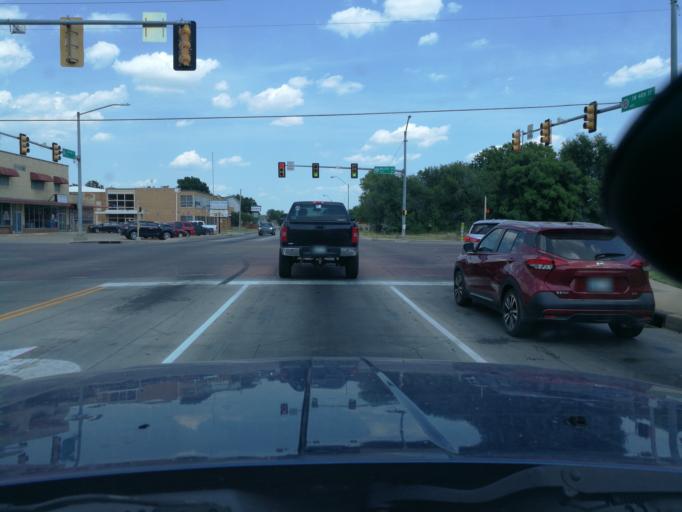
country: US
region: Oklahoma
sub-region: Oklahoma County
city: Oklahoma City
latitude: 35.4207
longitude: -97.5217
